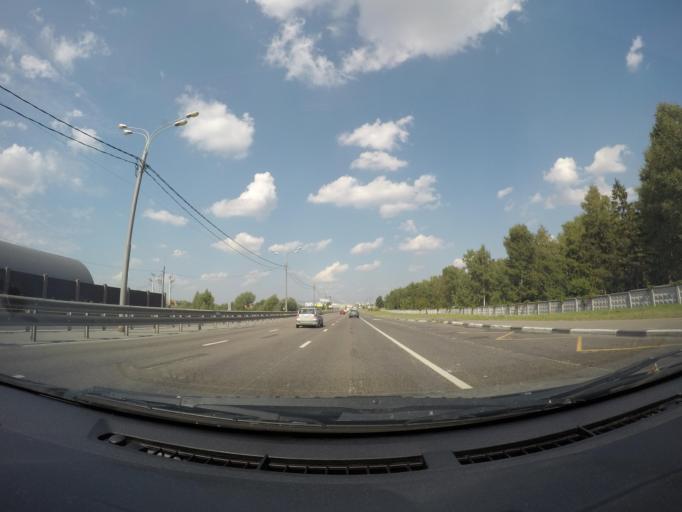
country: RU
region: Moscow
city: Businovo
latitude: 55.9080
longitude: 37.4938
